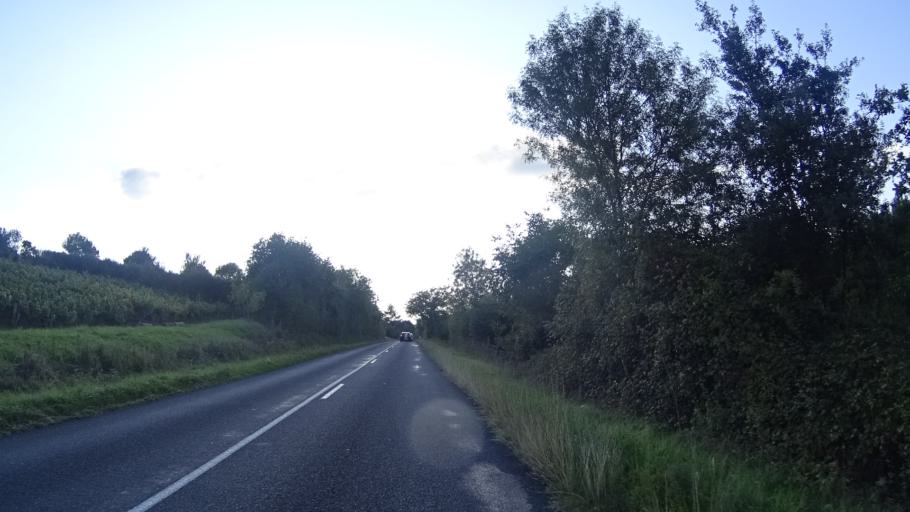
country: FR
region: Pays de la Loire
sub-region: Departement de Maine-et-Loire
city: Drain
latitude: 47.3453
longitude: -1.1907
